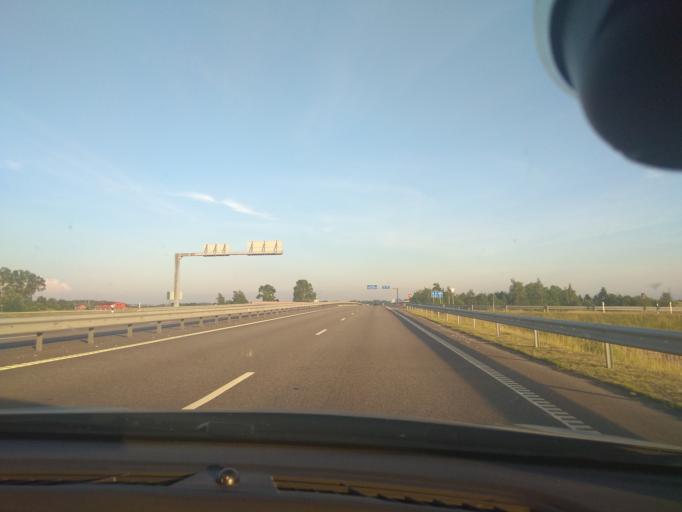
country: LT
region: Klaipedos apskritis
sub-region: Klaipeda
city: Klaipeda
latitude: 55.7937
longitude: 21.1404
